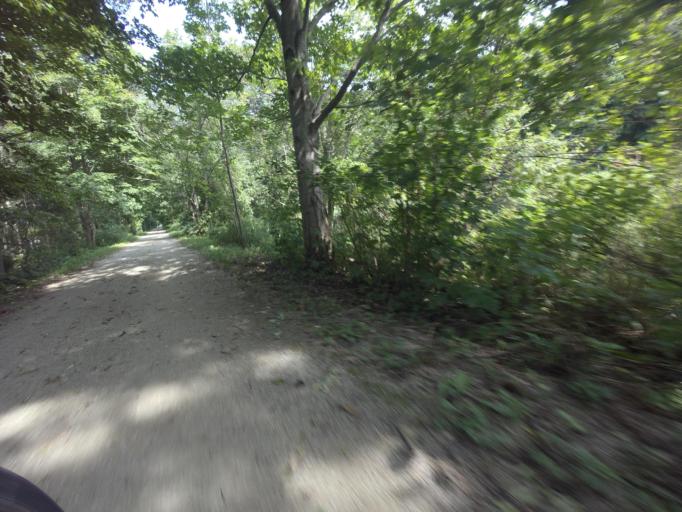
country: CA
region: Ontario
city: Waterloo
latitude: 43.6066
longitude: -80.6215
